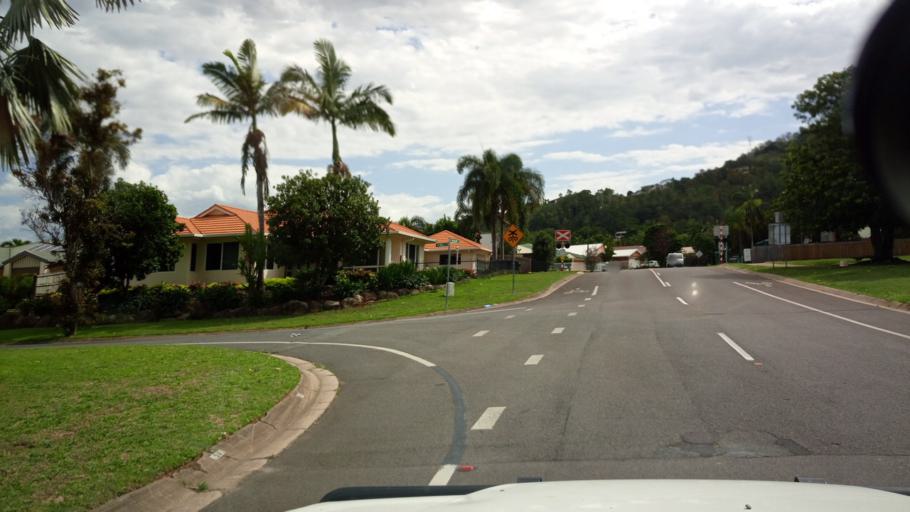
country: AU
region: Queensland
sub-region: Cairns
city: Woree
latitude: -16.9255
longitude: 145.7272
